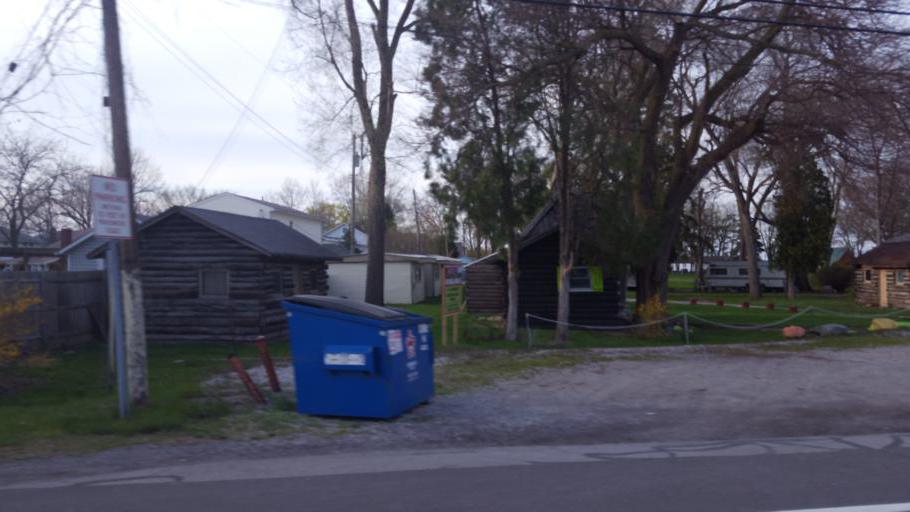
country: US
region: Ohio
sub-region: Erie County
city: Huron
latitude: 41.3832
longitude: -82.4636
